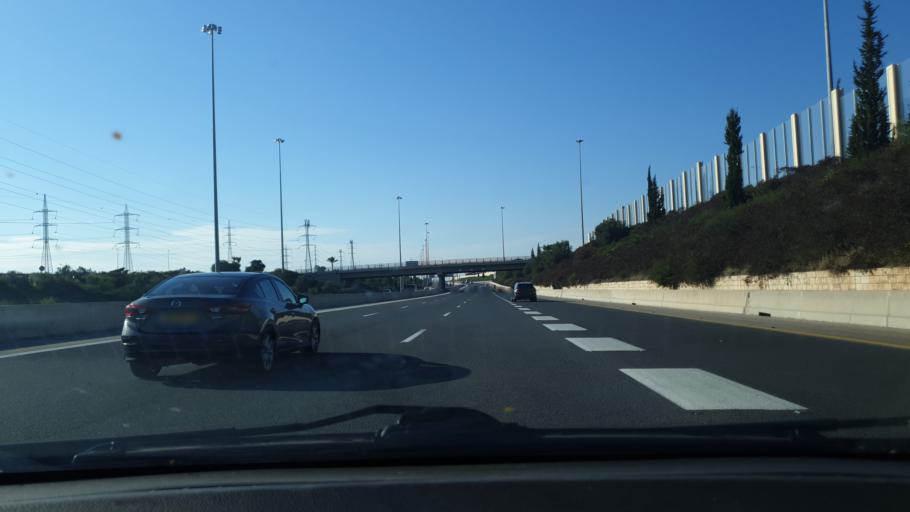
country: IL
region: Central District
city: Rishon LeZiyyon
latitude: 31.9618
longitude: 34.7700
